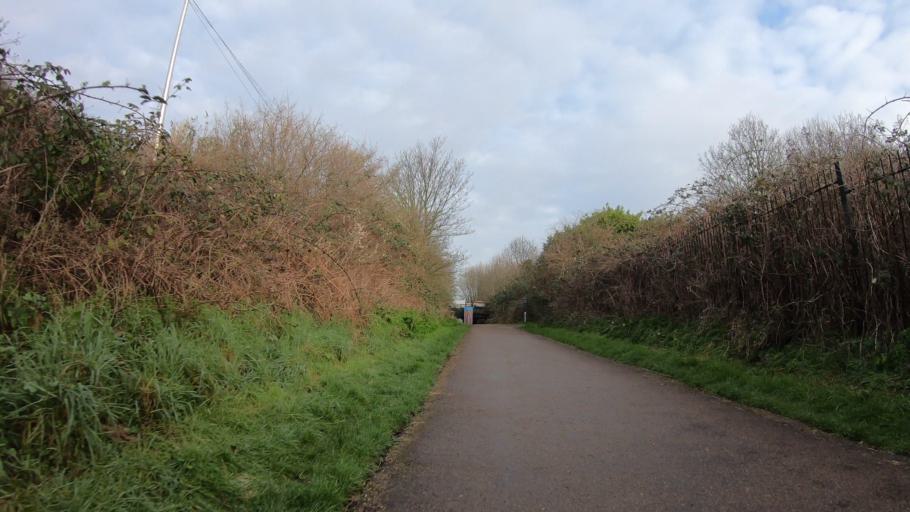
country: GB
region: England
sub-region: Greater London
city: Hackney
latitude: 51.5585
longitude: -0.0250
